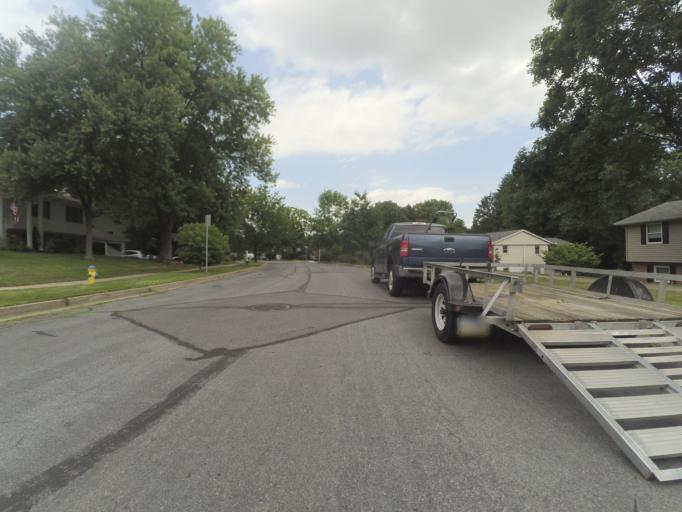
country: US
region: Pennsylvania
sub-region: Centre County
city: State College
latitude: 40.7770
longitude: -77.8617
